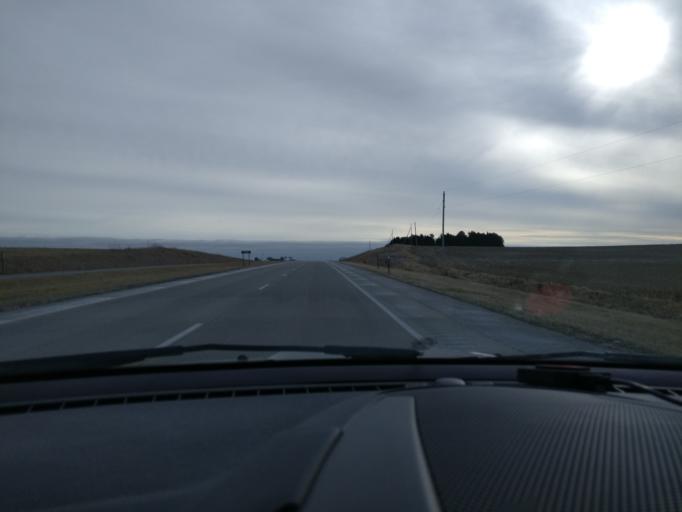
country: US
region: Nebraska
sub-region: Saunders County
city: Wahoo
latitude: 41.0885
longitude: -96.6402
